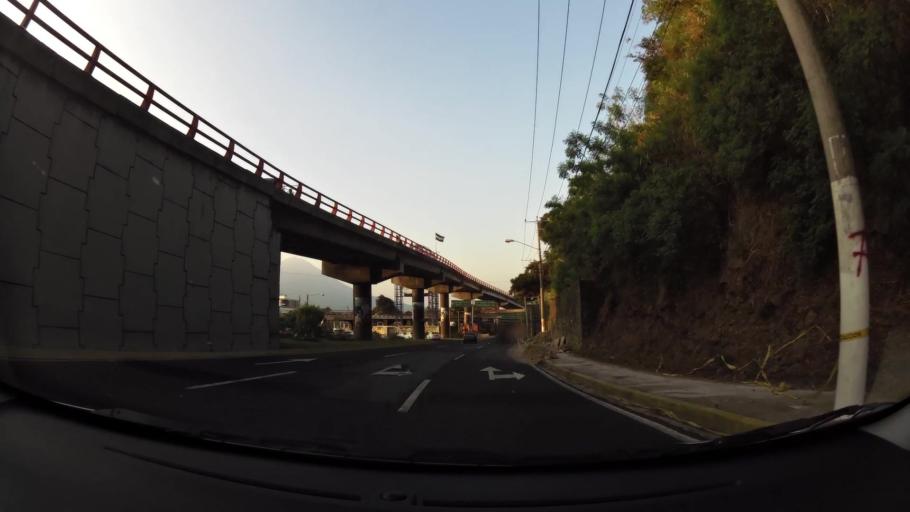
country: SV
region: San Salvador
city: San Salvador
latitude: 13.6837
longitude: -89.2179
